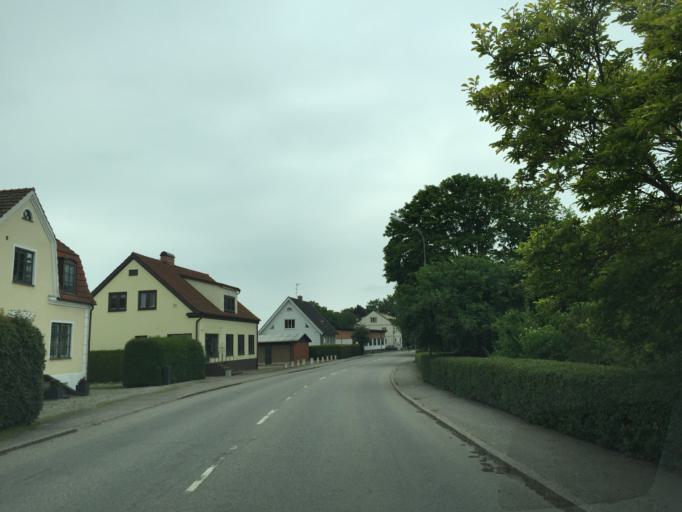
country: SE
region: Skane
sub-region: Ystads Kommun
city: Kopingebro
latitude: 55.4373
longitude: 14.1135
